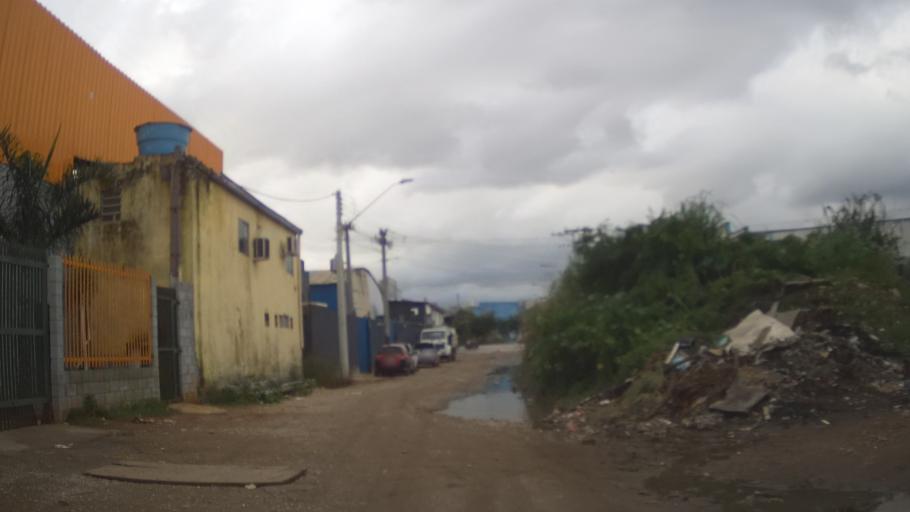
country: BR
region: Sao Paulo
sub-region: Guarulhos
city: Guarulhos
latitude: -23.4676
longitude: -46.4799
